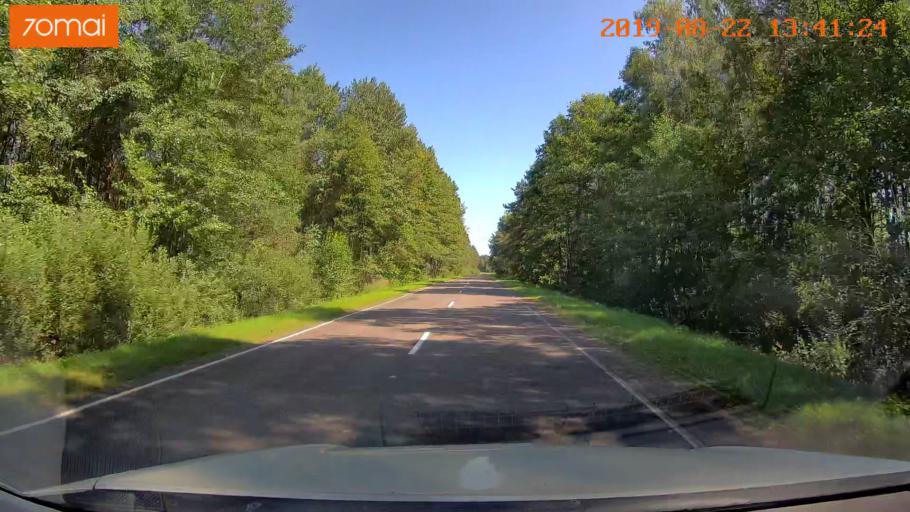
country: BY
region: Minsk
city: Staryya Darohi
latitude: 53.2386
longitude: 28.3963
